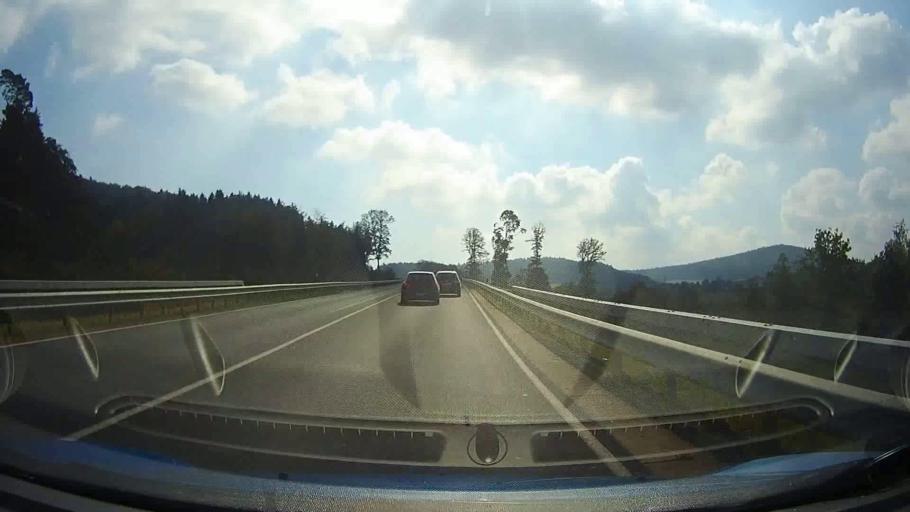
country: DE
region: Lower Saxony
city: Hardegsen
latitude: 51.6527
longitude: 9.7643
